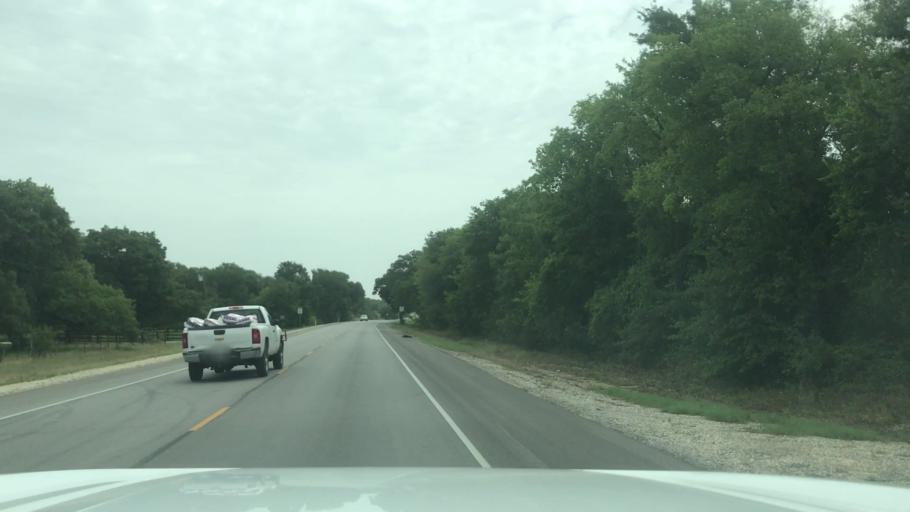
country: US
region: Texas
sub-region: Erath County
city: Dublin
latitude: 32.0876
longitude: -98.3051
